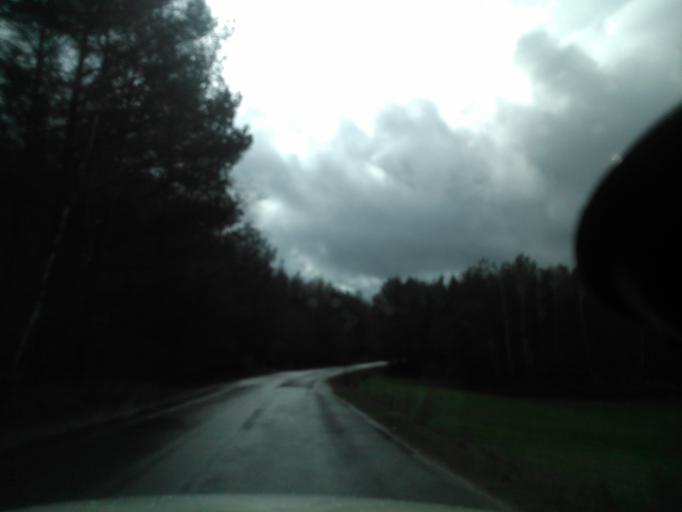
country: PL
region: Warmian-Masurian Voivodeship
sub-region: Powiat dzialdowski
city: Lidzbark
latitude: 53.2853
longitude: 19.8513
